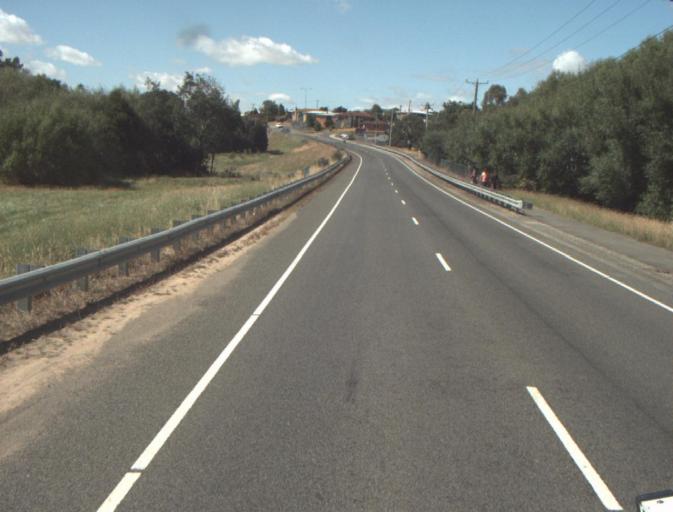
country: AU
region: Tasmania
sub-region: Launceston
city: Newstead
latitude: -41.4284
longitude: 147.1867
